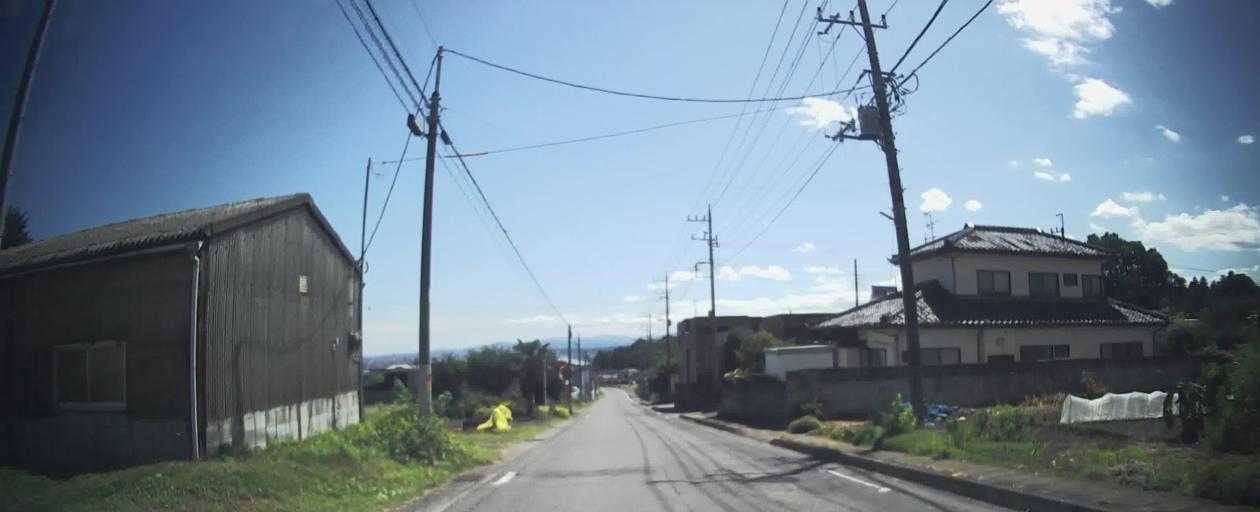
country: JP
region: Gunma
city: Kanekomachi
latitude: 36.4080
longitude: 138.9527
